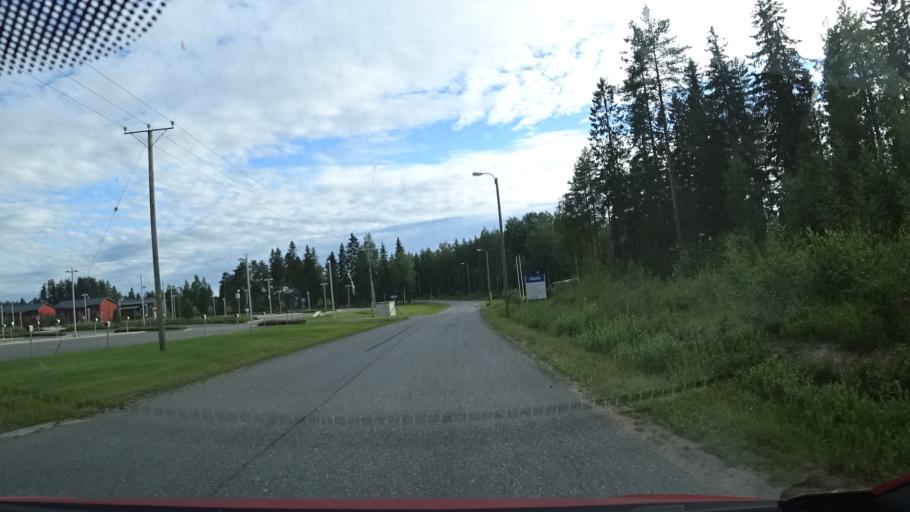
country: FI
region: Northern Ostrobothnia
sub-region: Oulu
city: Haukipudas
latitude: 65.1968
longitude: 25.4129
